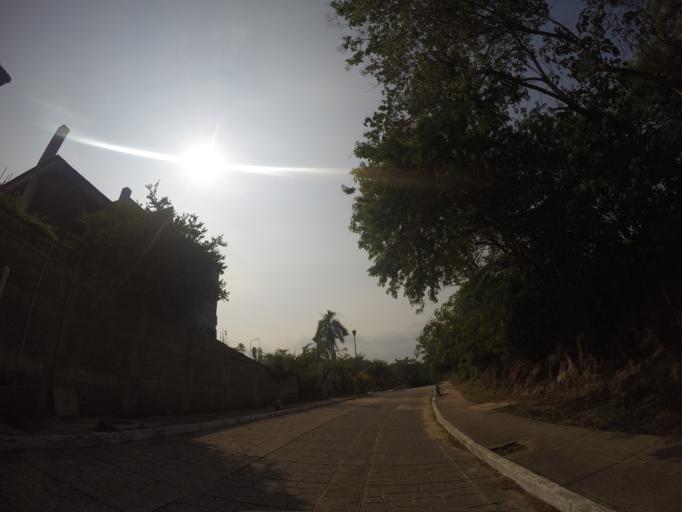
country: MX
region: Oaxaca
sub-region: Santa Maria Huatulco
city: Crucecita
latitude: 15.7552
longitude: -96.1274
